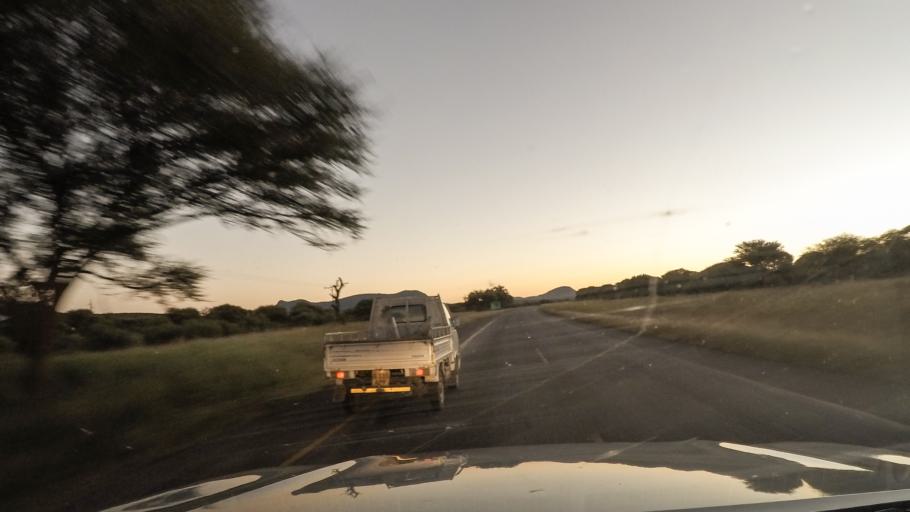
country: BW
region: South East
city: Otse
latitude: -25.0995
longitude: 25.7091
